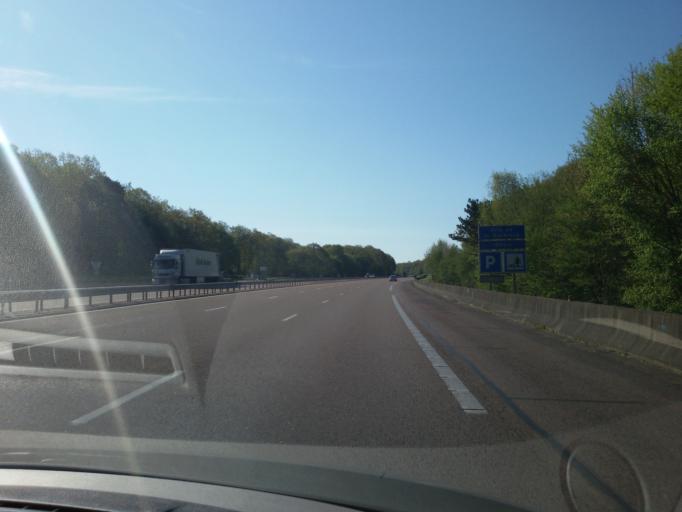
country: FR
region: Bourgogne
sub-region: Departement de l'Yonne
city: Aillant-sur-Tholon
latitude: 47.9207
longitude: 3.2848
